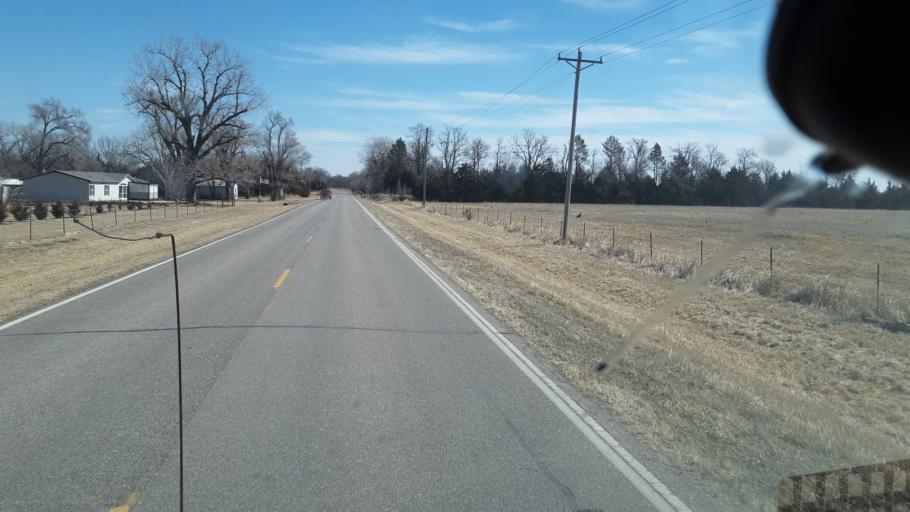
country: US
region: Kansas
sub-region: Reno County
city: Buhler
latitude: 38.1593
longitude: -97.8600
